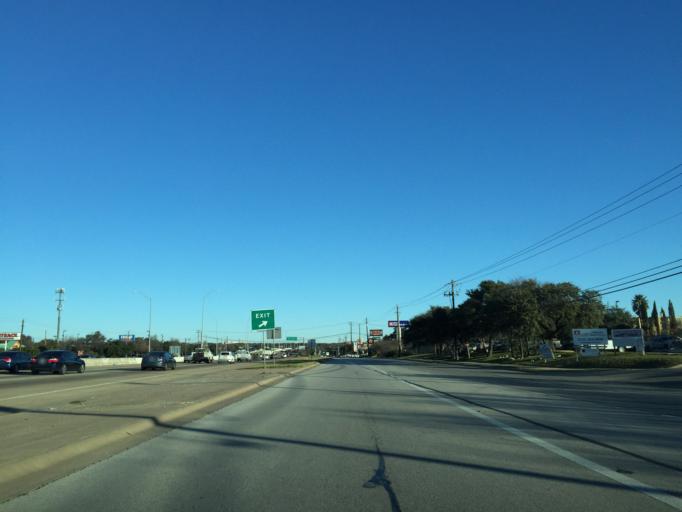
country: US
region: Texas
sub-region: Williamson County
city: Jollyville
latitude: 30.4140
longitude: -97.7456
